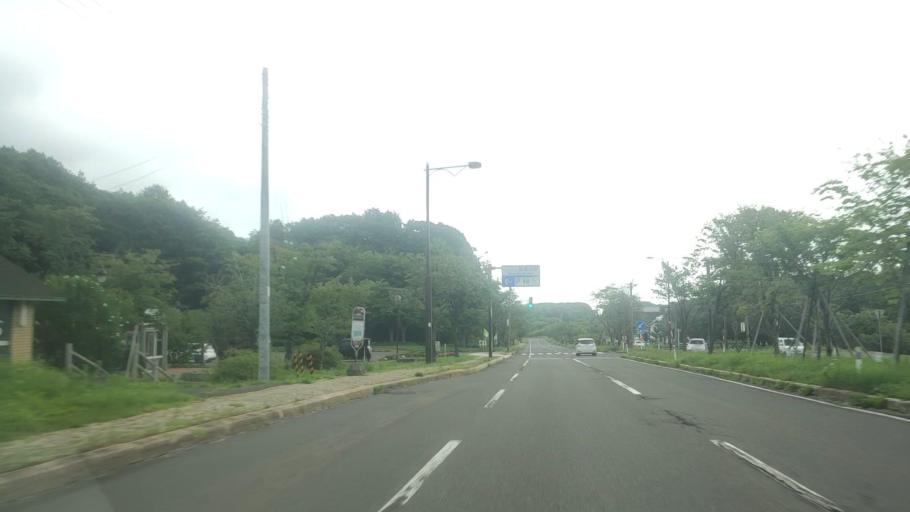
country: JP
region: Hokkaido
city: Shiraoi
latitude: 42.4667
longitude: 141.1670
